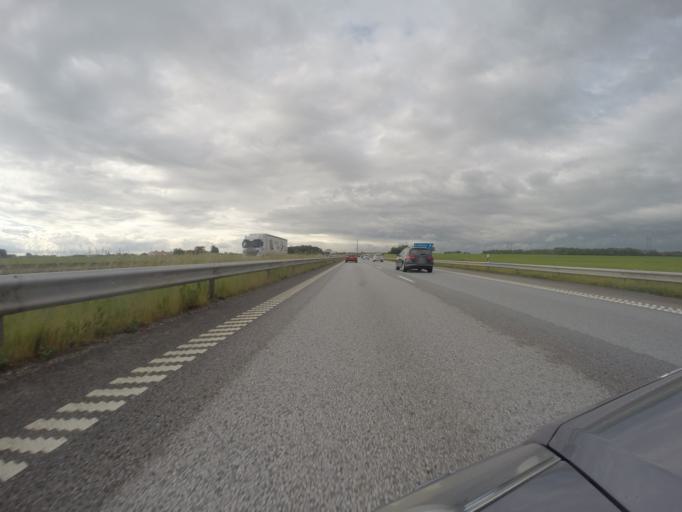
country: SE
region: Skane
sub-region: Lomma Kommun
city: Lomma
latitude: 55.7183
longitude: 13.0921
